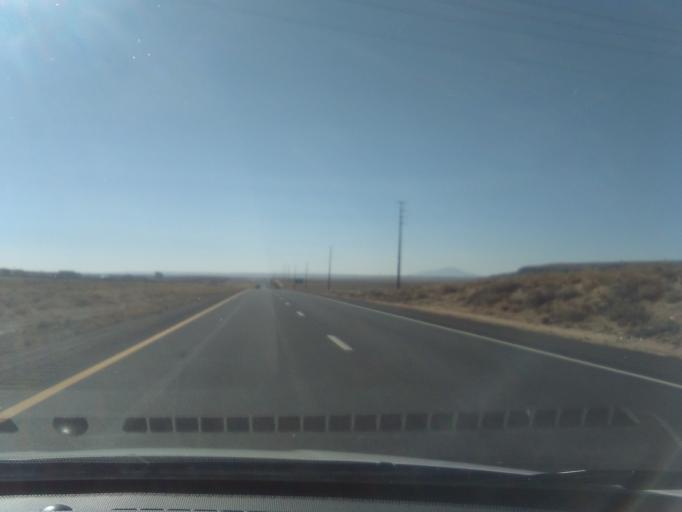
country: US
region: New Mexico
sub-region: Valencia County
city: Los Lunas
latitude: 34.7998
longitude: -106.7677
